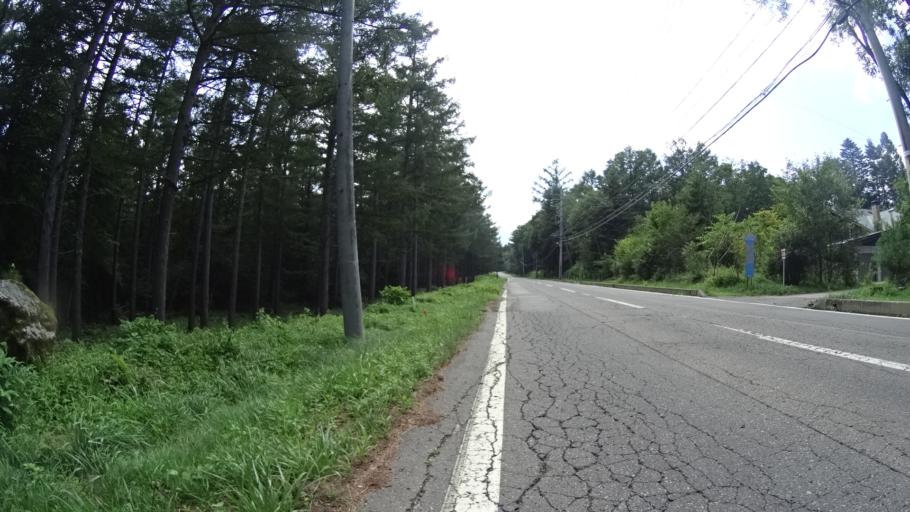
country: JP
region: Nagano
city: Saku
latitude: 36.0567
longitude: 138.4347
